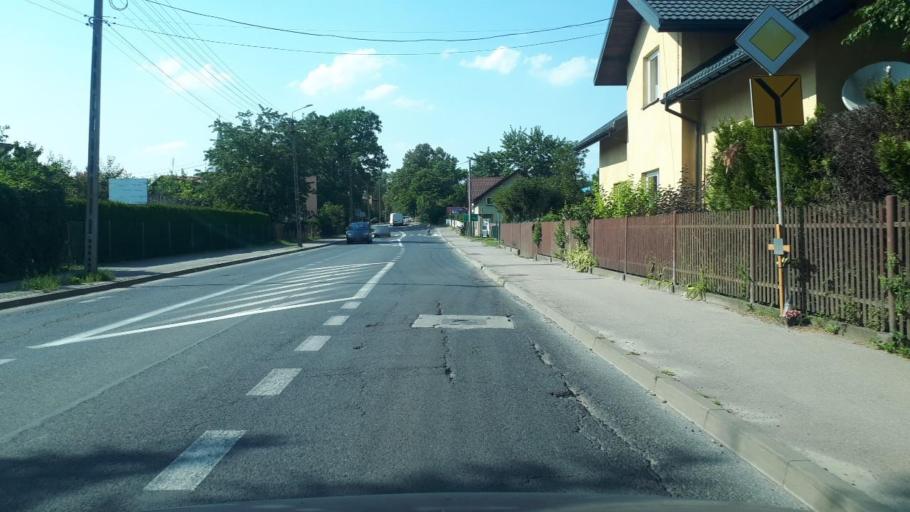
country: PL
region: Silesian Voivodeship
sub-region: Powiat bielski
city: Czechowice-Dziedzice
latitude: 49.9165
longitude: 18.9947
